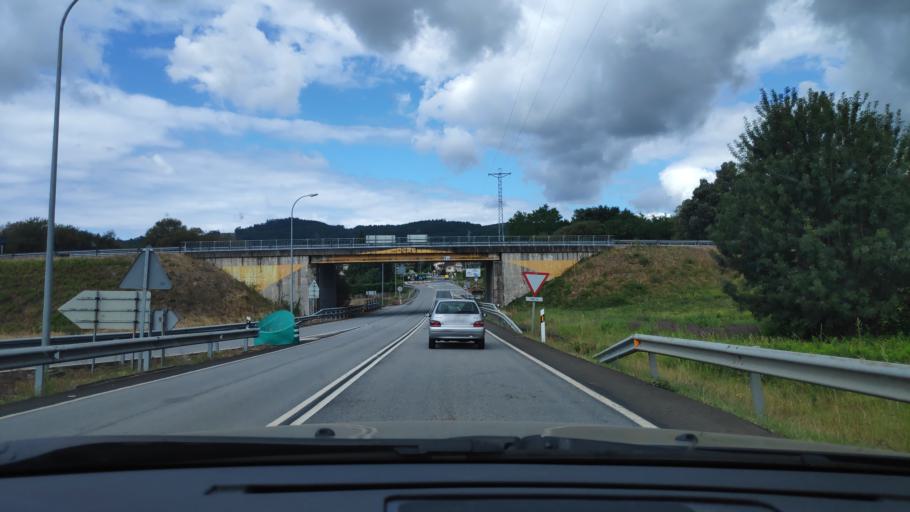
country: ES
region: Galicia
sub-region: Provincia de Pontevedra
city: Portas
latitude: 42.5954
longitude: -8.6843
